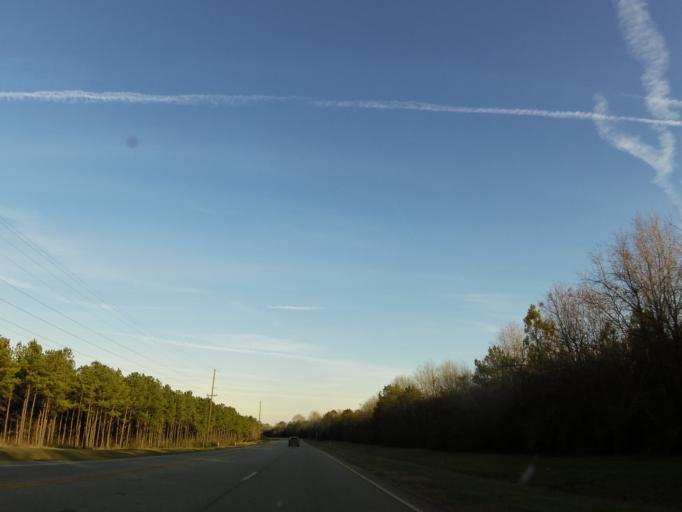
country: US
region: Georgia
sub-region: Sumter County
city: Americus
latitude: 32.0557
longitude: -84.3163
